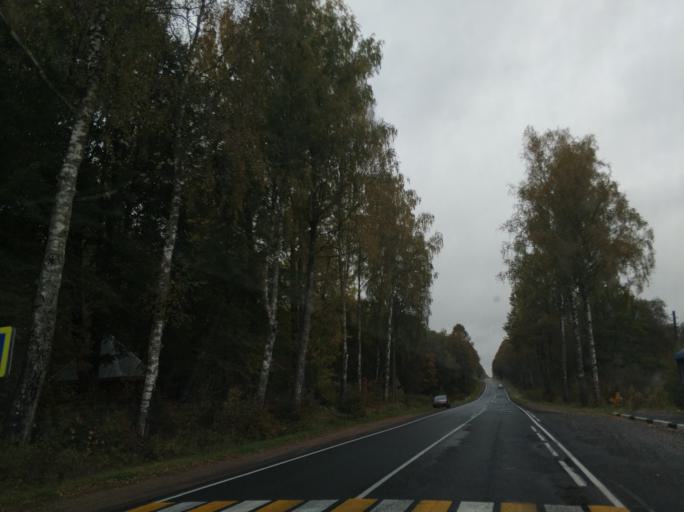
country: RU
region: Pskov
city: Opochka
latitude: 56.5558
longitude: 28.6320
